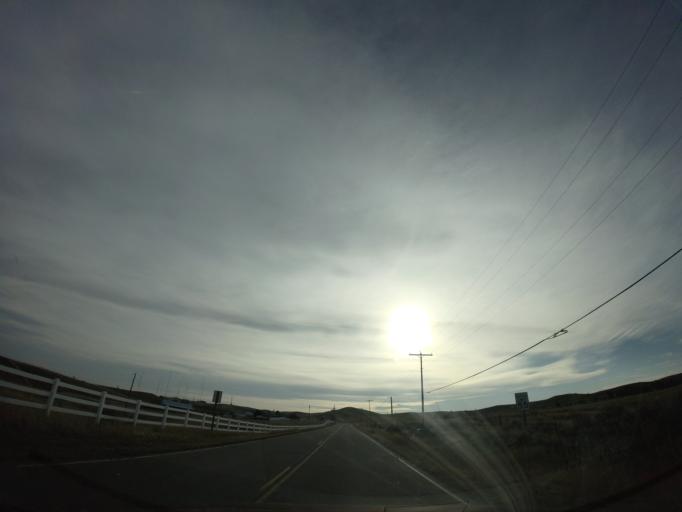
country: US
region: Montana
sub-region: Yellowstone County
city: Billings
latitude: 45.7800
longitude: -108.4614
